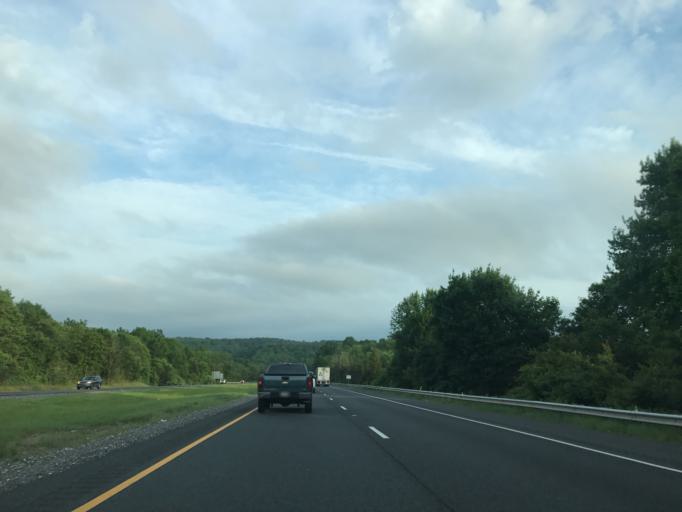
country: US
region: Pennsylvania
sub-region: York County
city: New Freedom
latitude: 39.6215
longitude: -76.6669
